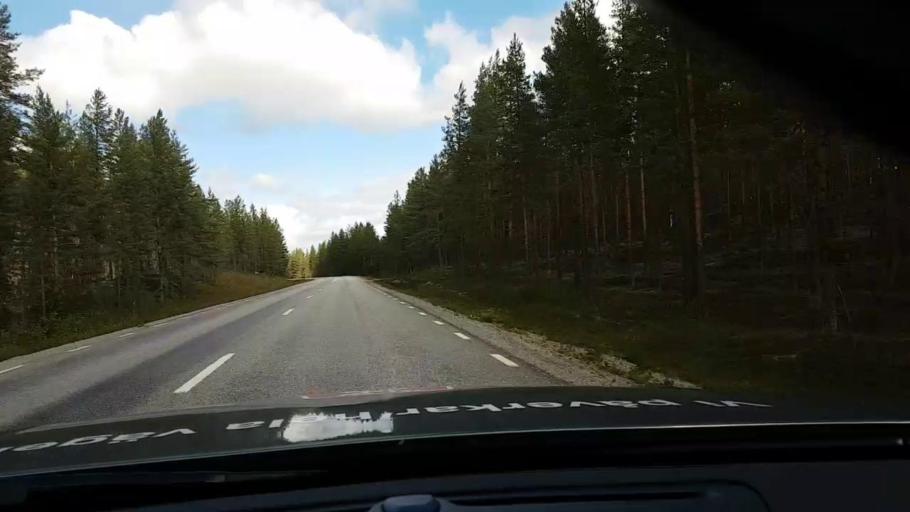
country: SE
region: Vaesternorrland
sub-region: OErnskoeldsviks Kommun
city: Bredbyn
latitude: 63.6135
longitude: 17.9038
